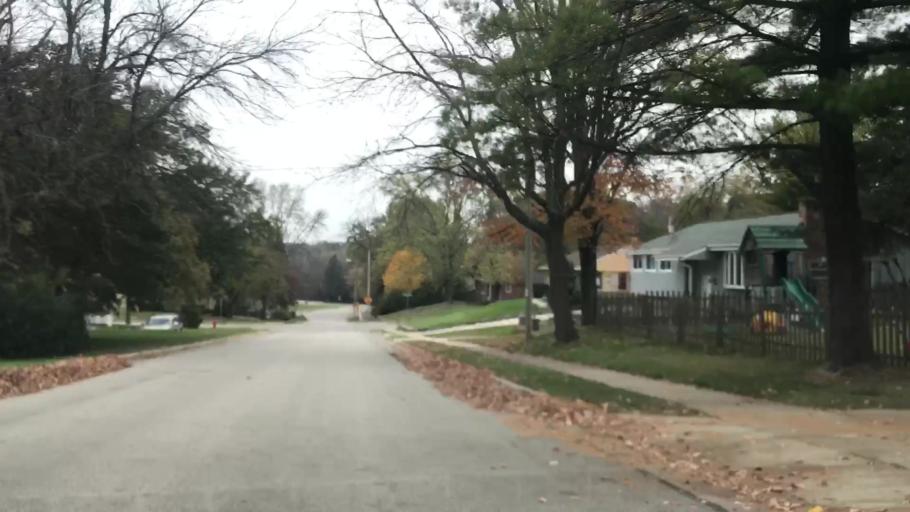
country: US
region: Wisconsin
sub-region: Waukesha County
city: Menomonee Falls
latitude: 43.1778
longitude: -88.1085
